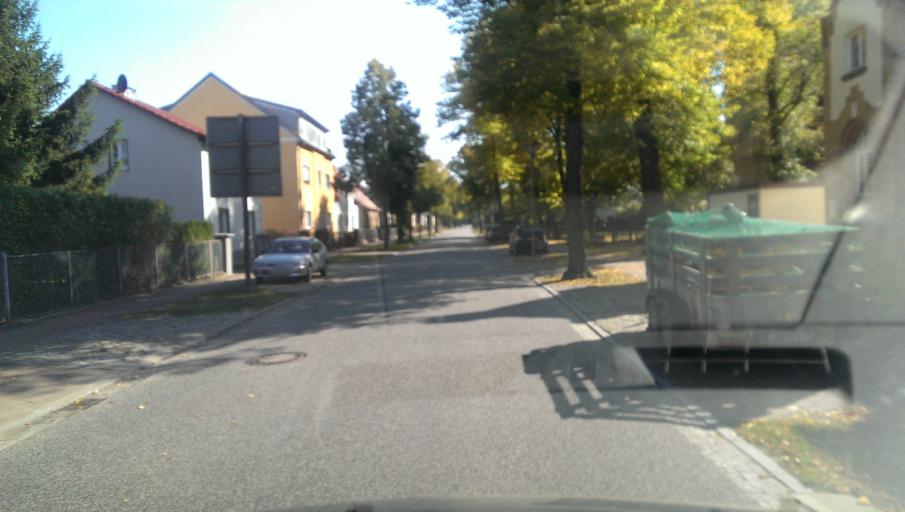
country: DE
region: Brandenburg
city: Halbe
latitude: 52.1054
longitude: 13.7028
